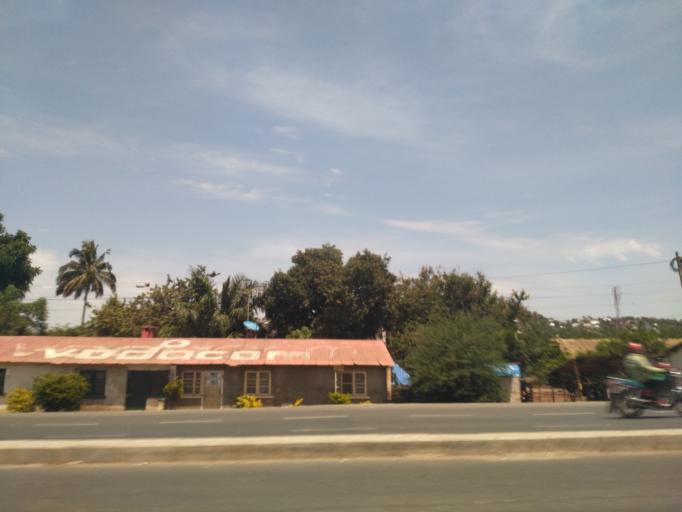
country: TZ
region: Mwanza
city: Mwanza
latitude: -2.5029
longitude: 32.9021
